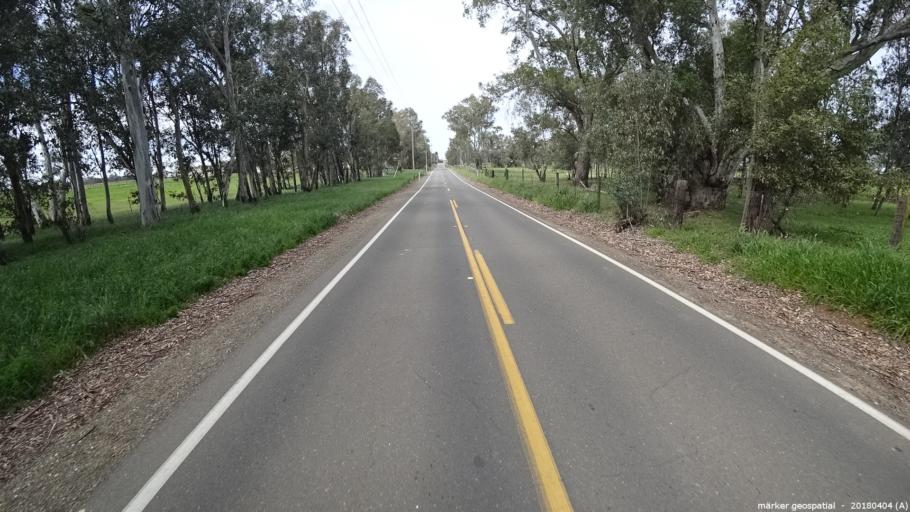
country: US
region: California
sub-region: Sacramento County
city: Clay
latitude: 38.3214
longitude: -121.1635
